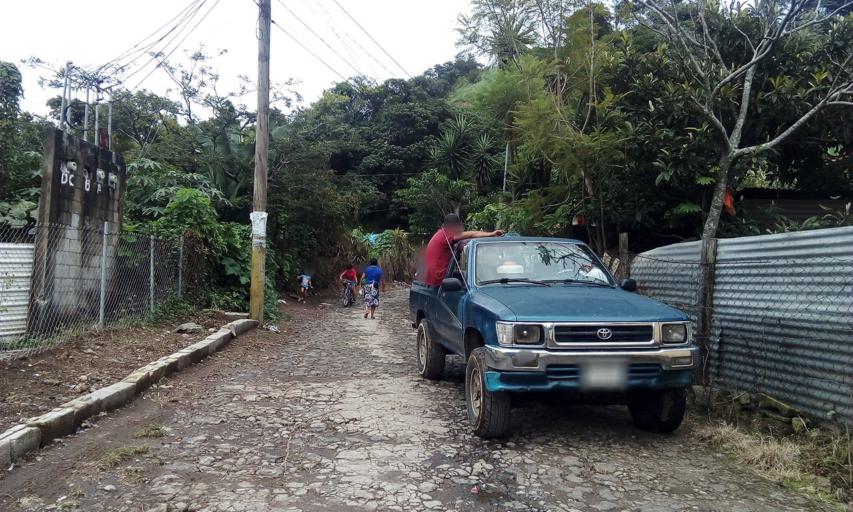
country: GT
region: Escuintla
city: San Vicente Pacaya
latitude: 14.3333
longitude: -90.6033
